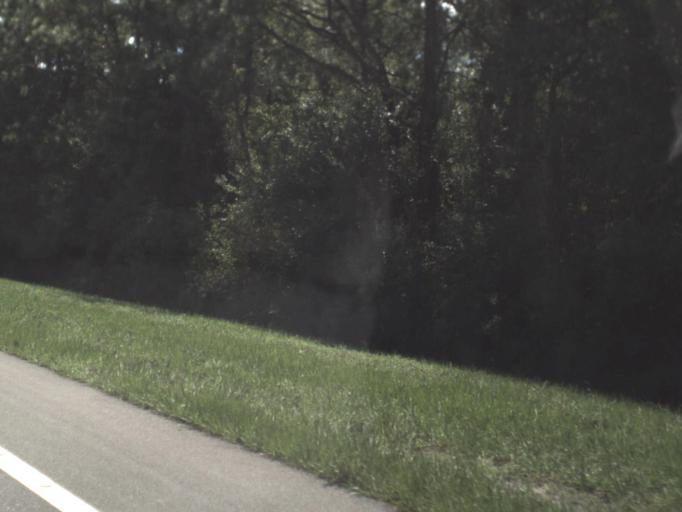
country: US
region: Florida
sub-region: Sarasota County
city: The Meadows
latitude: 27.4296
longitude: -82.3807
